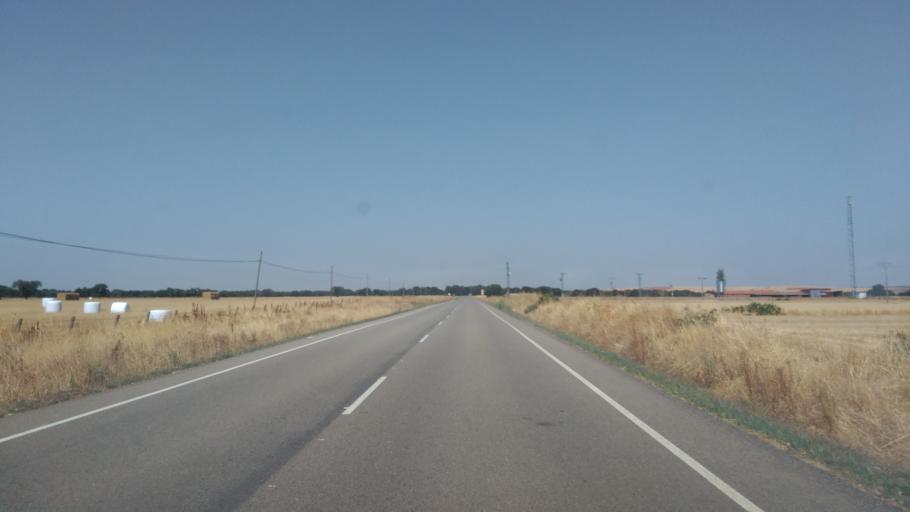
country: ES
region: Castille and Leon
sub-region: Provincia de Salamanca
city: Abusejo
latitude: 40.7188
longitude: -6.1485
